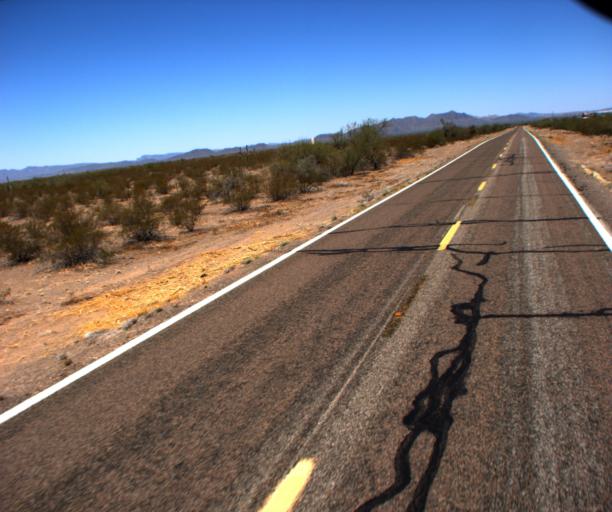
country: US
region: Arizona
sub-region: Pima County
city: Ajo
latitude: 32.2378
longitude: -112.7205
